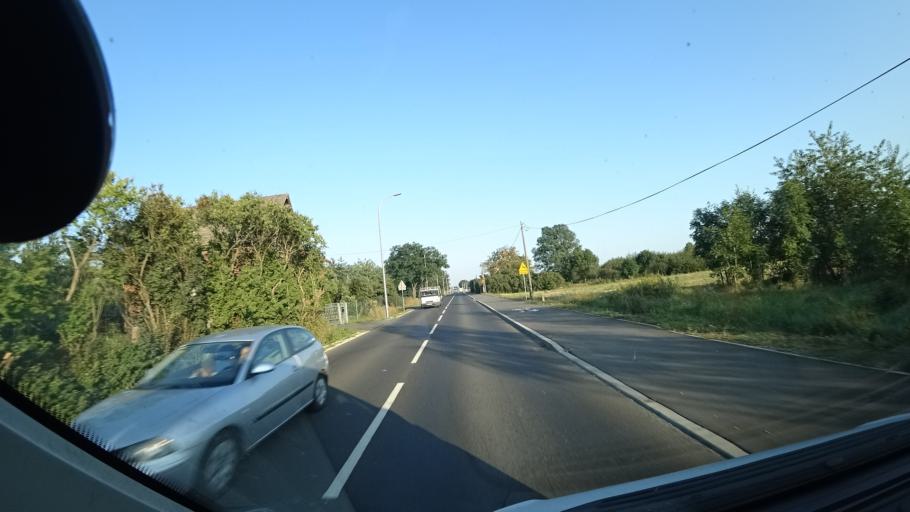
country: PL
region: Opole Voivodeship
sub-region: Powiat kedzierzynsko-kozielski
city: Bierawa
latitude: 50.2923
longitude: 18.2545
